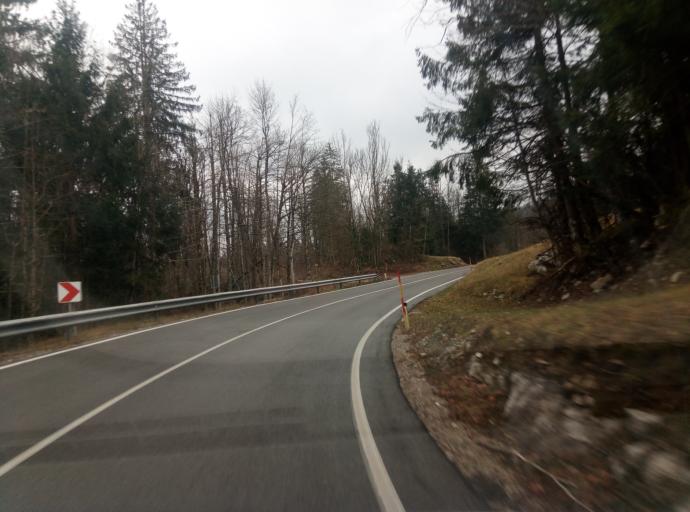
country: SI
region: Idrija
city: Idrija
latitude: 45.9523
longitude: 14.0794
